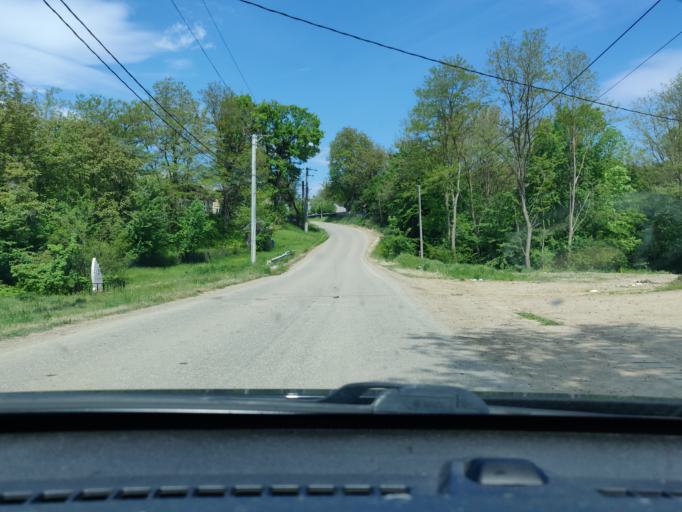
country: RO
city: Vizantea-Manastireasca
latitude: 45.9798
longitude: 26.7990
